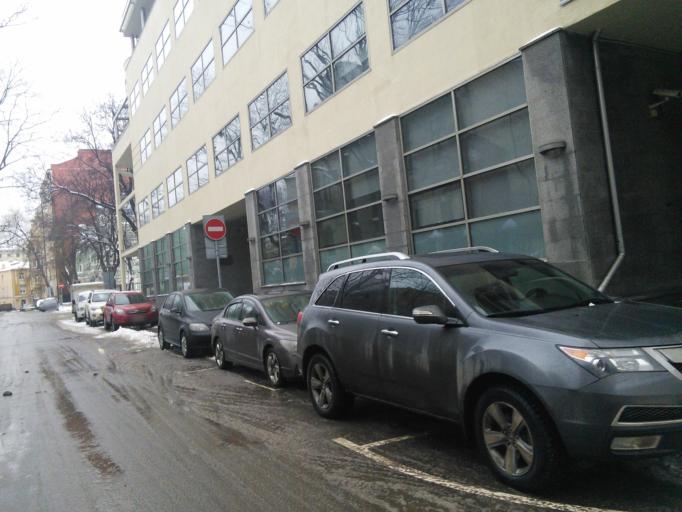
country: RU
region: Moscow
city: Moscow
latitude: 55.7658
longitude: 37.6426
